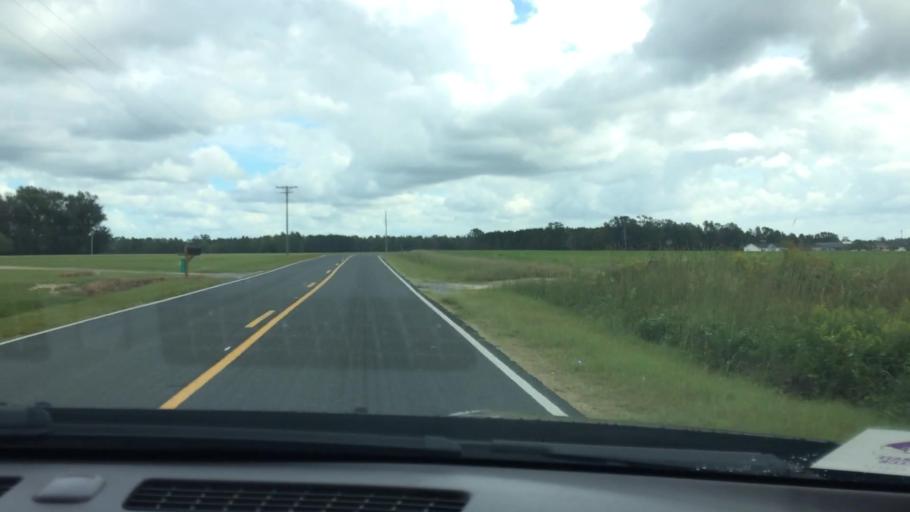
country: US
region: North Carolina
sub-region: Greene County
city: Maury
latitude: 35.5173
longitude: -77.5278
